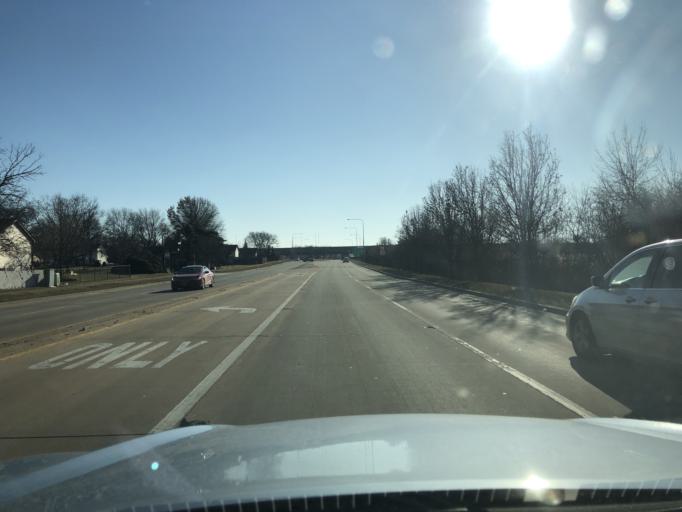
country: US
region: Illinois
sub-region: DuPage County
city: Roselle
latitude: 41.9962
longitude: -88.0461
